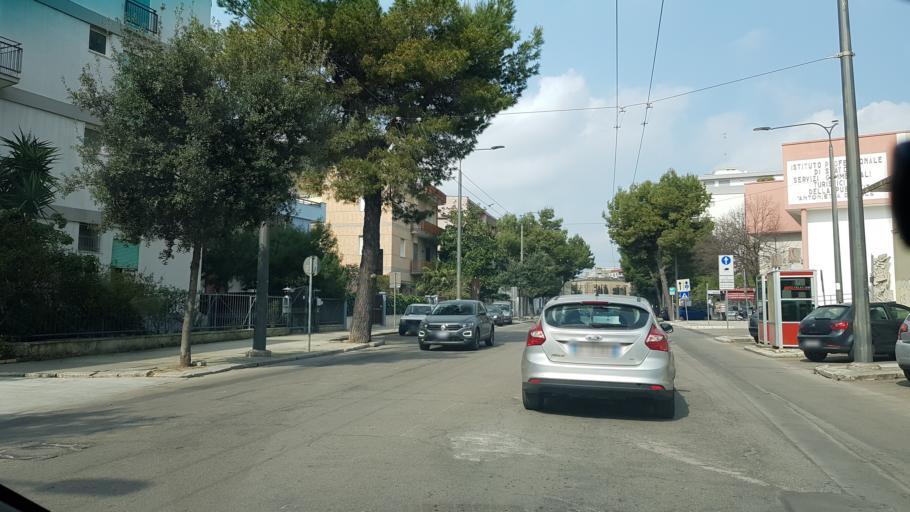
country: IT
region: Apulia
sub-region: Provincia di Lecce
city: Lecce
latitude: 40.3440
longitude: 18.1726
